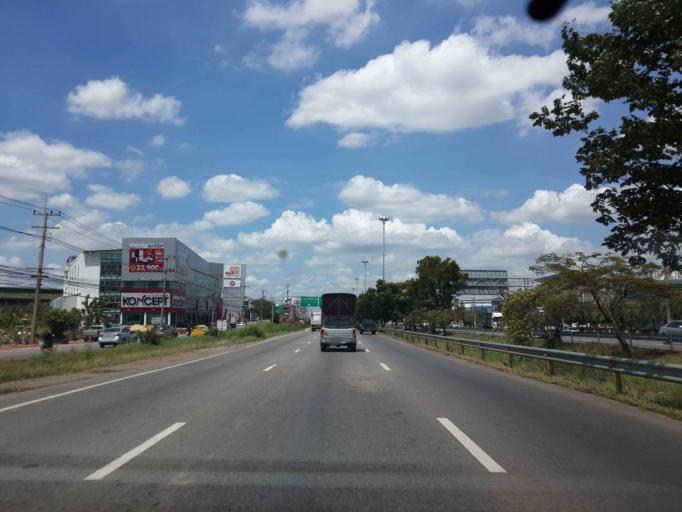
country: TH
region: Bangkok
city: Bang Bon
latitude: 13.6067
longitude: 100.3741
